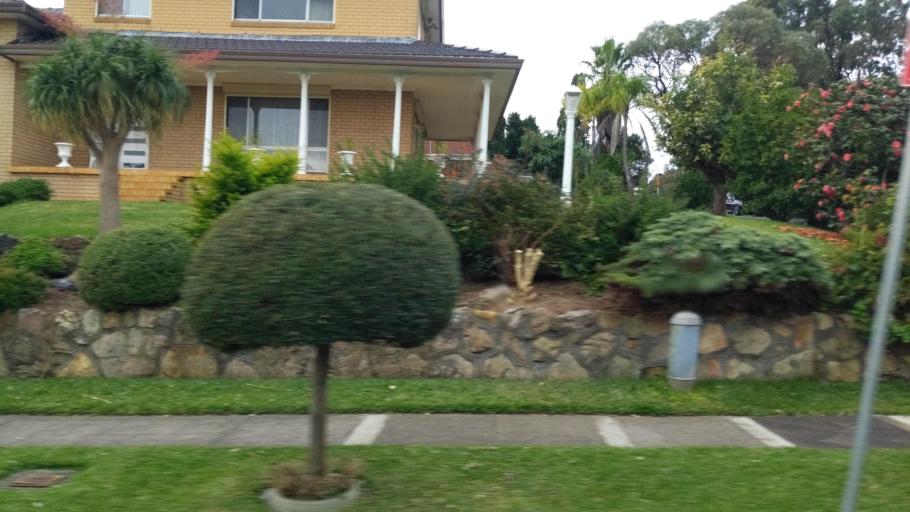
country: AU
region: New South Wales
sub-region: Blacktown
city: Blacktown
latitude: -33.7462
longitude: 150.9300
